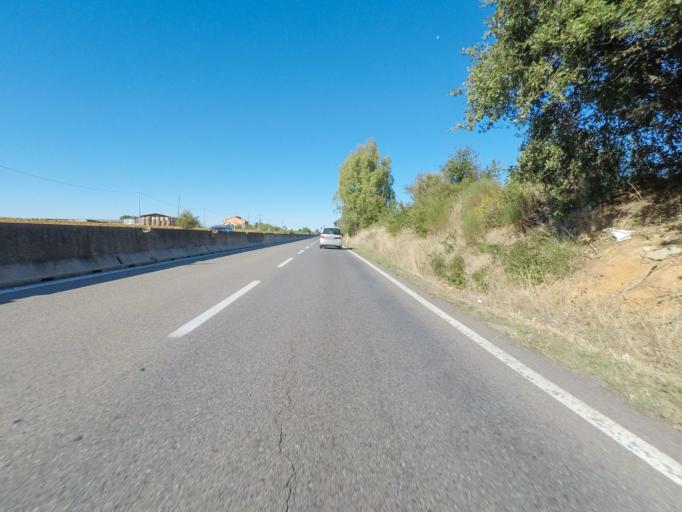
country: IT
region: Tuscany
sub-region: Provincia di Grosseto
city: Grosseto
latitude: 42.6973
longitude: 11.1378
